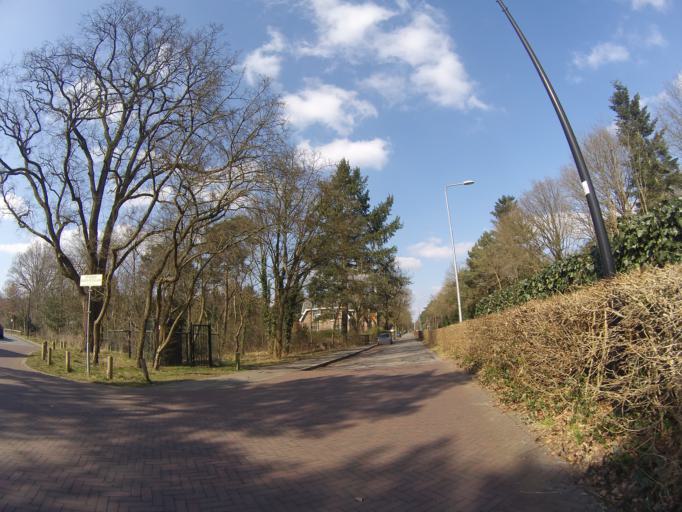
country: NL
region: Utrecht
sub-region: Gemeente Zeist
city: Zeist
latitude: 52.1447
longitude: 5.2386
